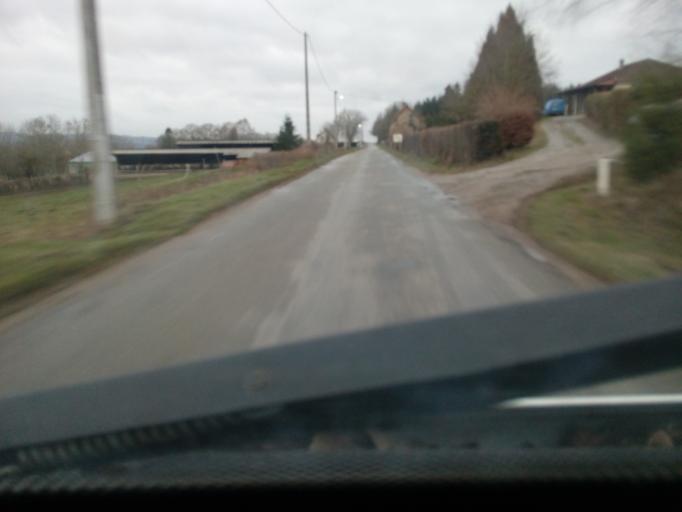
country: FR
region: Limousin
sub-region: Departement de la Creuse
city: Felletin
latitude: 45.8751
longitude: 2.1968
